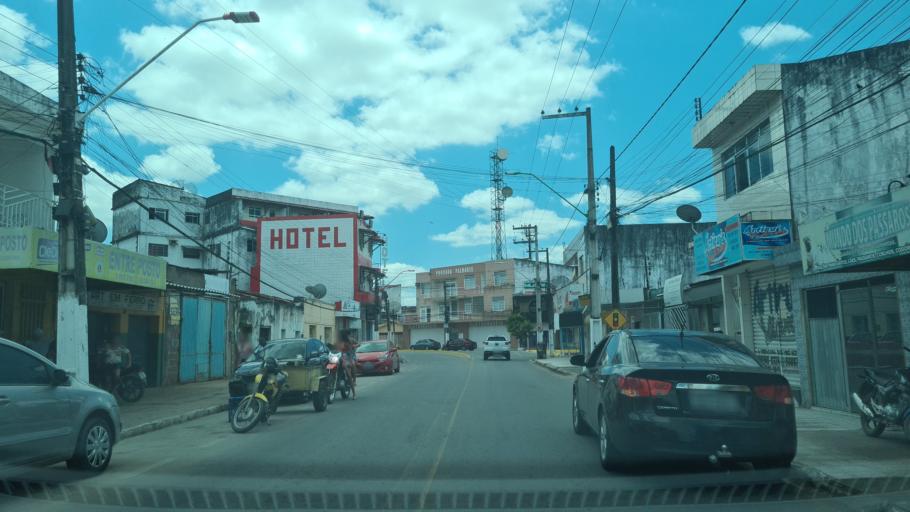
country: BR
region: Alagoas
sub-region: Uniao Dos Palmares
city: Uniao dos Palmares
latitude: -9.1600
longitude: -36.0305
